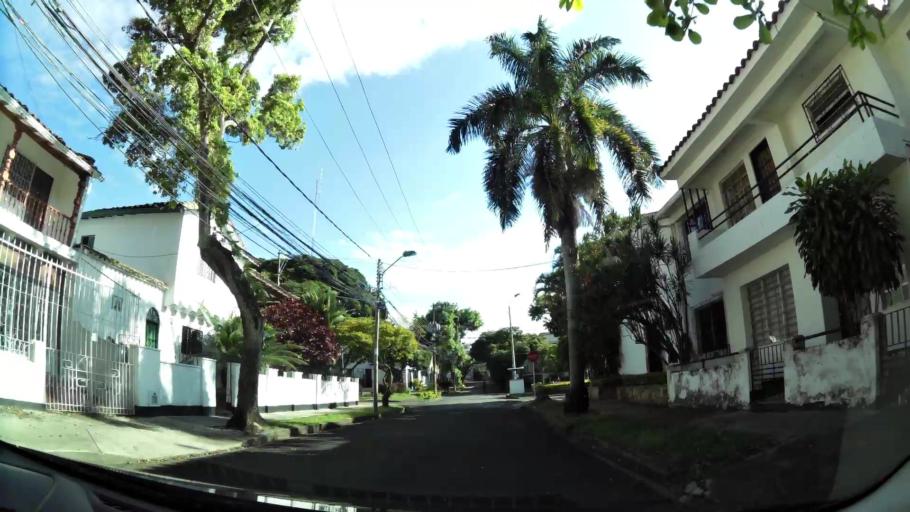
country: CO
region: Valle del Cauca
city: Cali
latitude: 3.4380
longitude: -76.5396
